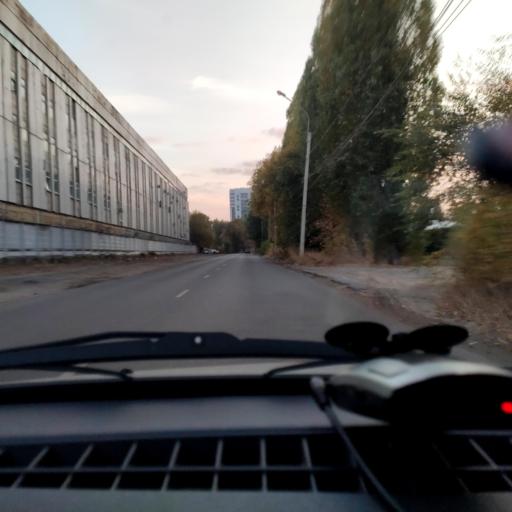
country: RU
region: Voronezj
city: Voronezh
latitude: 51.6791
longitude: 39.1455
